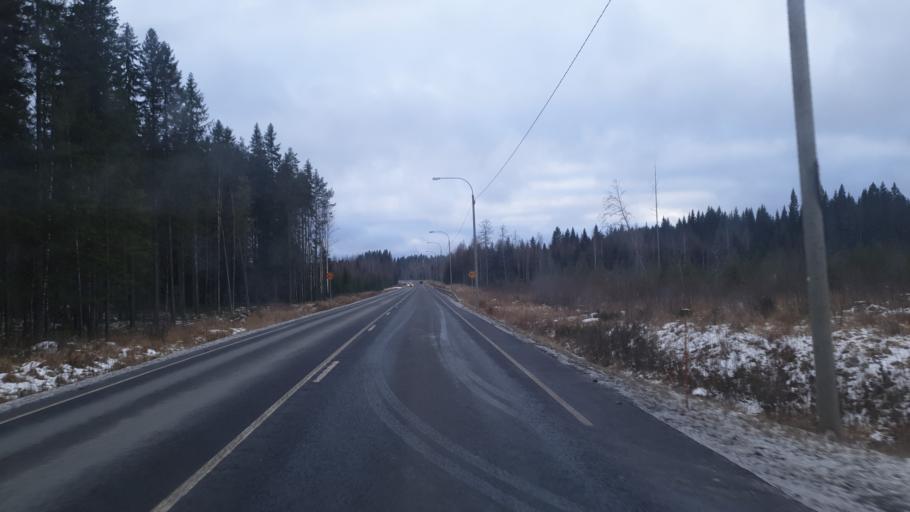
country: FI
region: Northern Savo
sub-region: Kuopio
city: Kuopio
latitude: 62.6841
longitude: 27.5739
